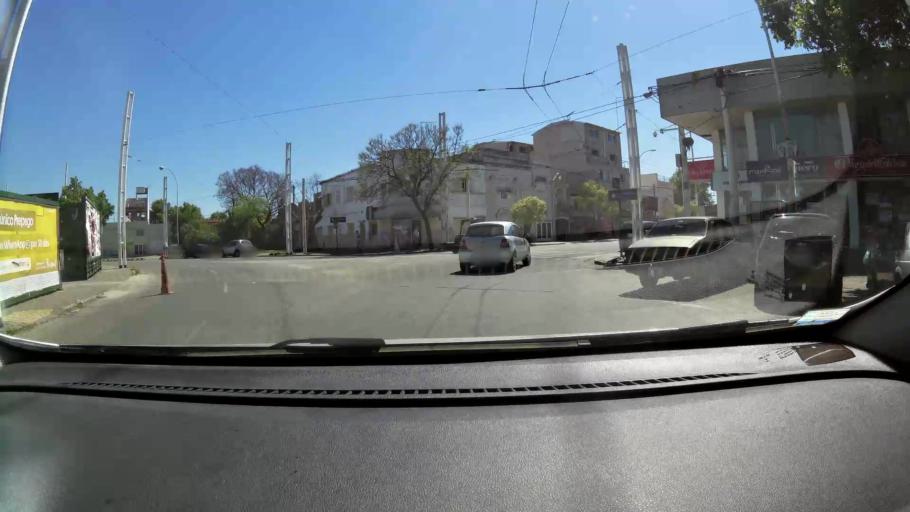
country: AR
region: Cordoba
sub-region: Departamento de Capital
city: Cordoba
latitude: -31.4231
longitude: -64.1526
